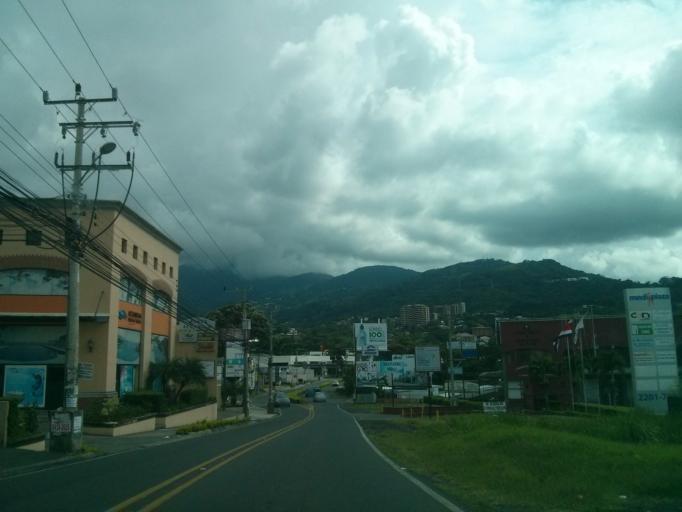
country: CR
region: San Jose
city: San Rafael
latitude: 9.9394
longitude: -84.1516
